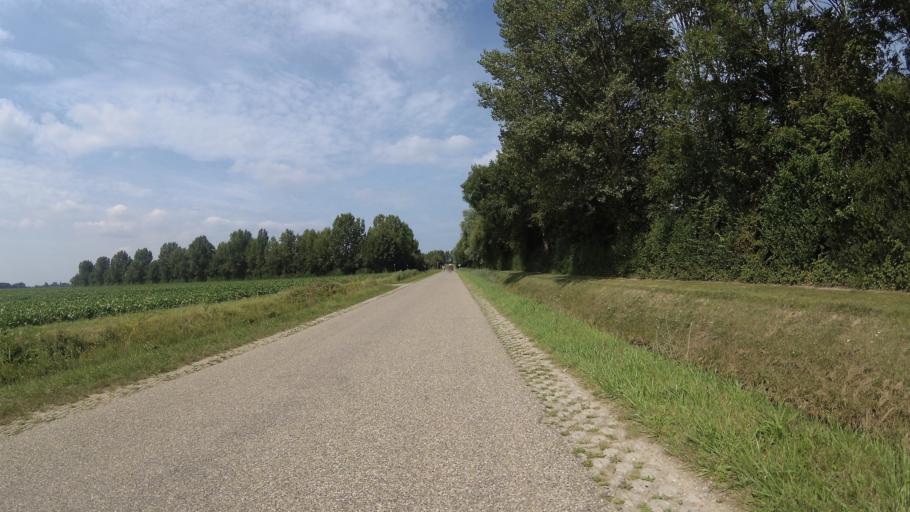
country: NL
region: Zeeland
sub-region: Gemeente Noord-Beveland
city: Kamperland
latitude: 51.5878
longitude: 3.7258
